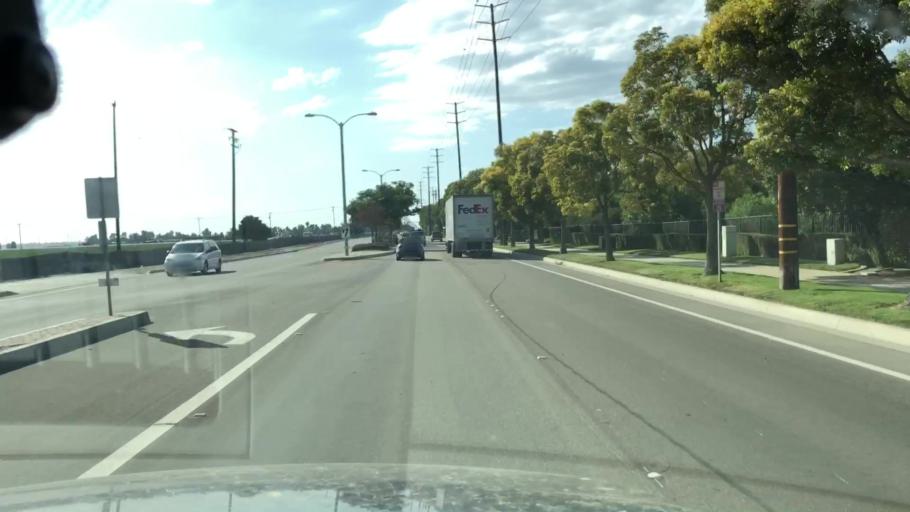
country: US
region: California
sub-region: Ventura County
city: Camarillo
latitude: 34.2055
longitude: -119.0290
